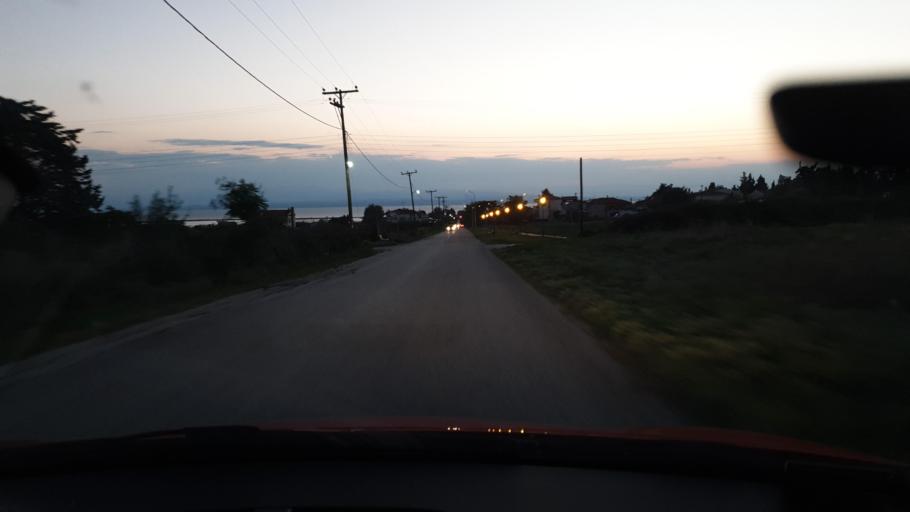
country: GR
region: Central Macedonia
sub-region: Nomos Thessalonikis
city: Agia Triada
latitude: 40.4967
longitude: 22.8400
